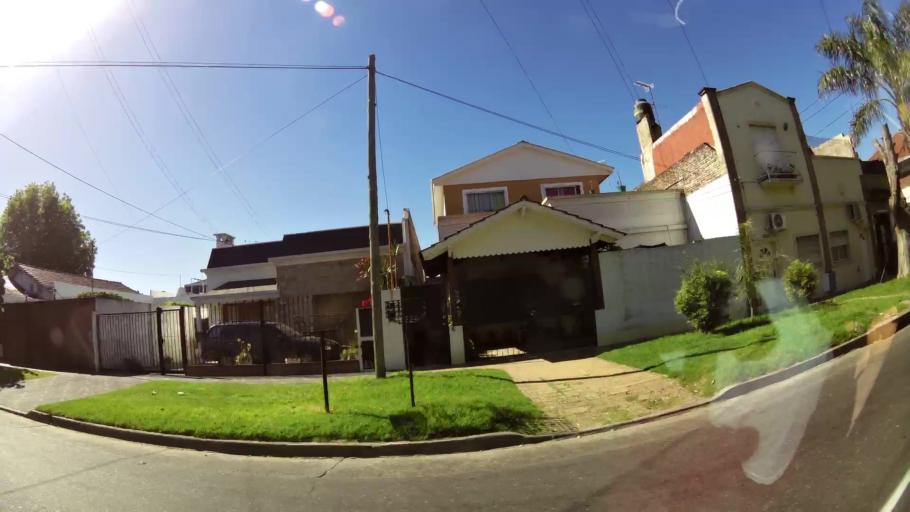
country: AR
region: Buenos Aires
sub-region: Partido de General San Martin
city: General San Martin
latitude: -34.5381
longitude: -58.5203
